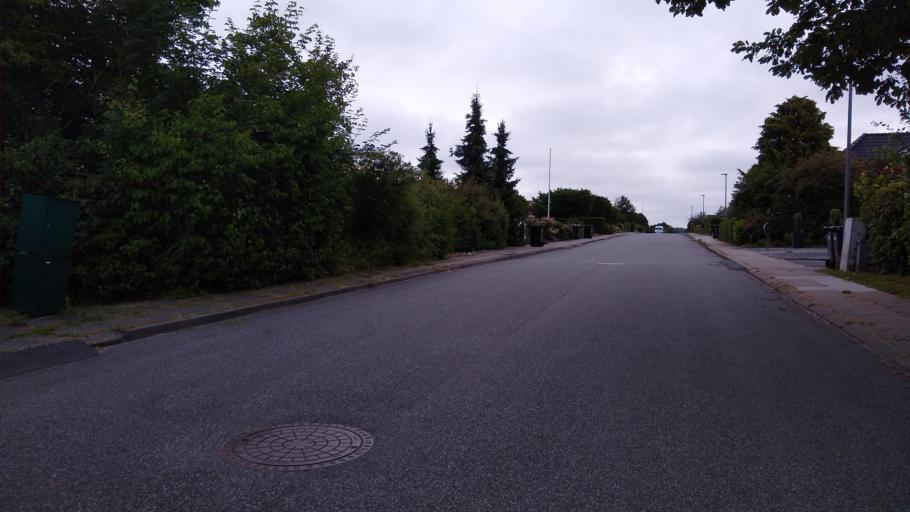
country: DK
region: South Denmark
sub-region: Vejle Kommune
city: Brejning
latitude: 55.6624
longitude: 9.6674
